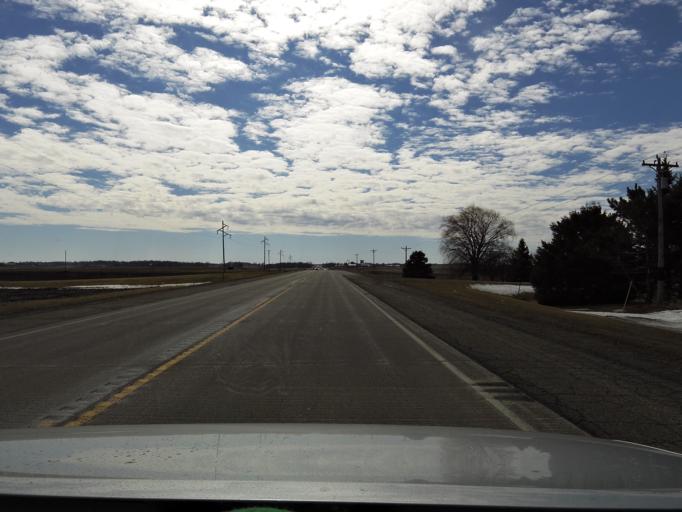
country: US
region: Minnesota
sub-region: Le Sueur County
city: New Prague
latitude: 44.5171
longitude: -93.5857
